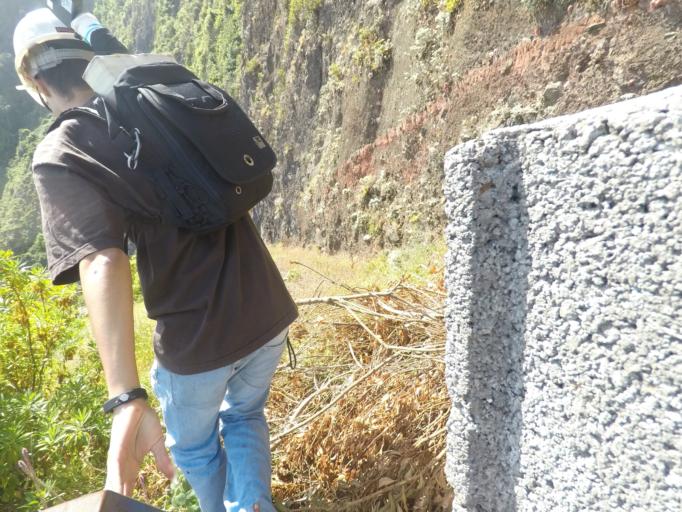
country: PT
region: Madeira
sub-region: Sao Vicente
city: Sao Vicente
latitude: 32.8159
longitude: -17.0949
